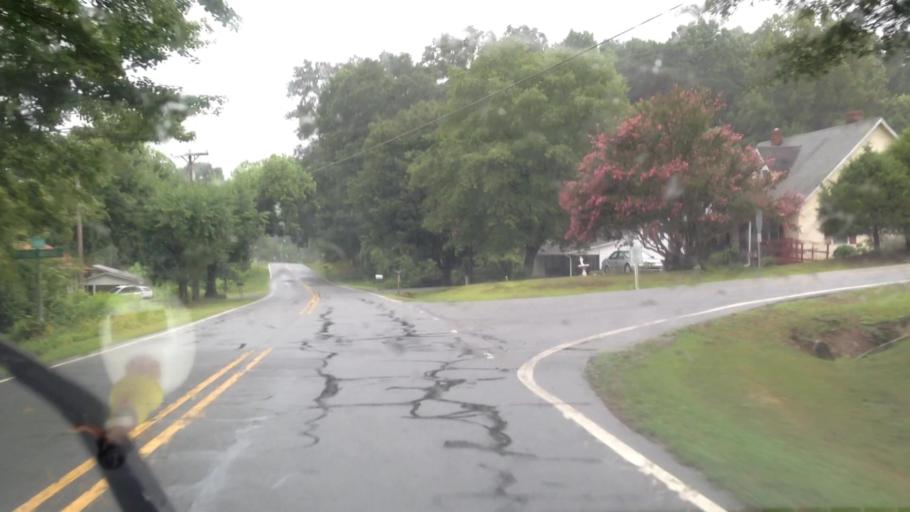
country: US
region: North Carolina
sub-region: Stokes County
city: Walnut Cove
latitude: 36.3248
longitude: -80.0493
